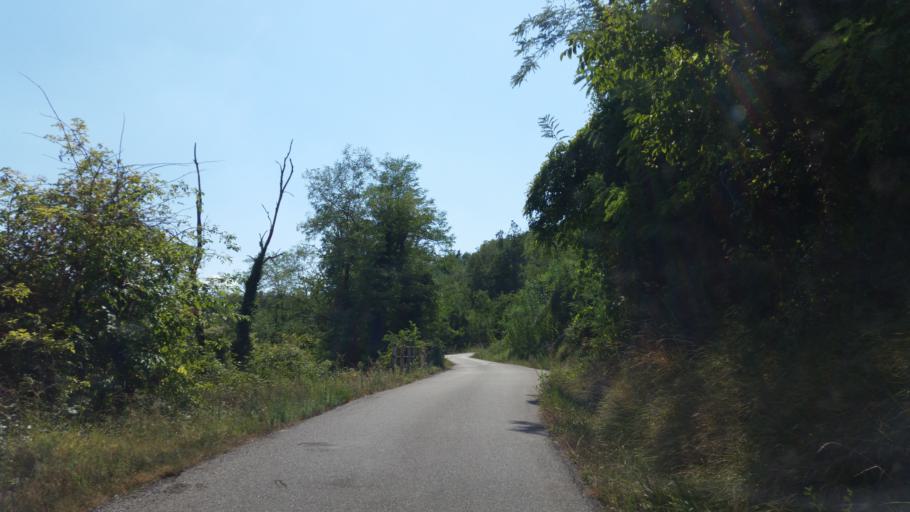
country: IT
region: Piedmont
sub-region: Provincia di Cuneo
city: Trezzo Tinella
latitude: 44.6765
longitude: 8.1009
